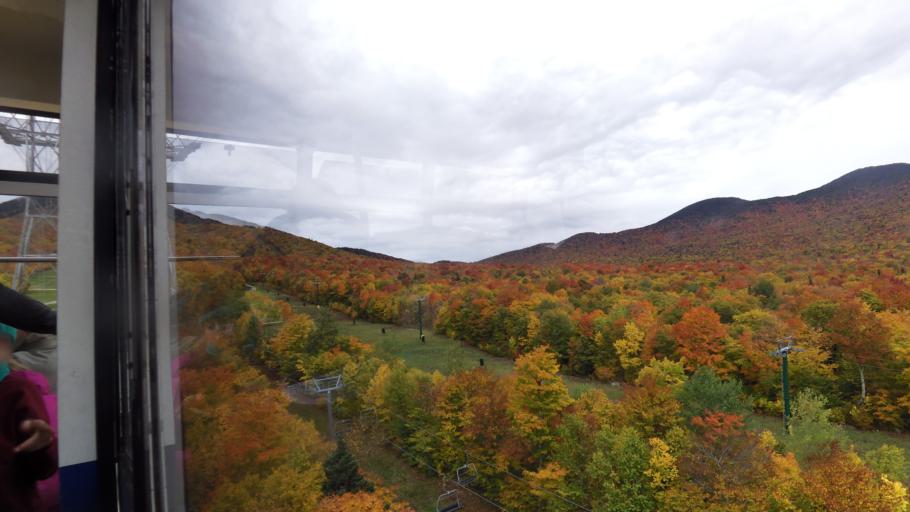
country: US
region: Vermont
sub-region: Franklin County
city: Richford
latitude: 44.9394
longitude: -72.5058
